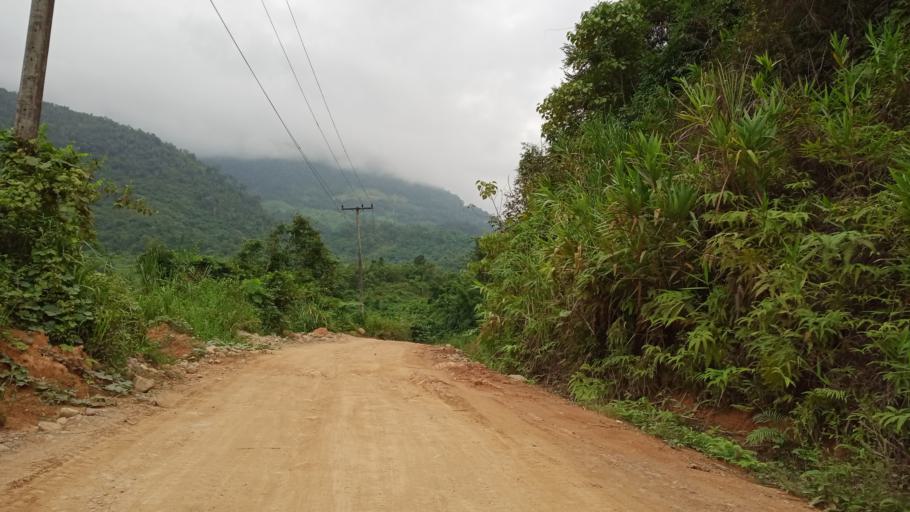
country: LA
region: Xiangkhoang
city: Phonsavan
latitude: 19.0921
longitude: 102.9858
